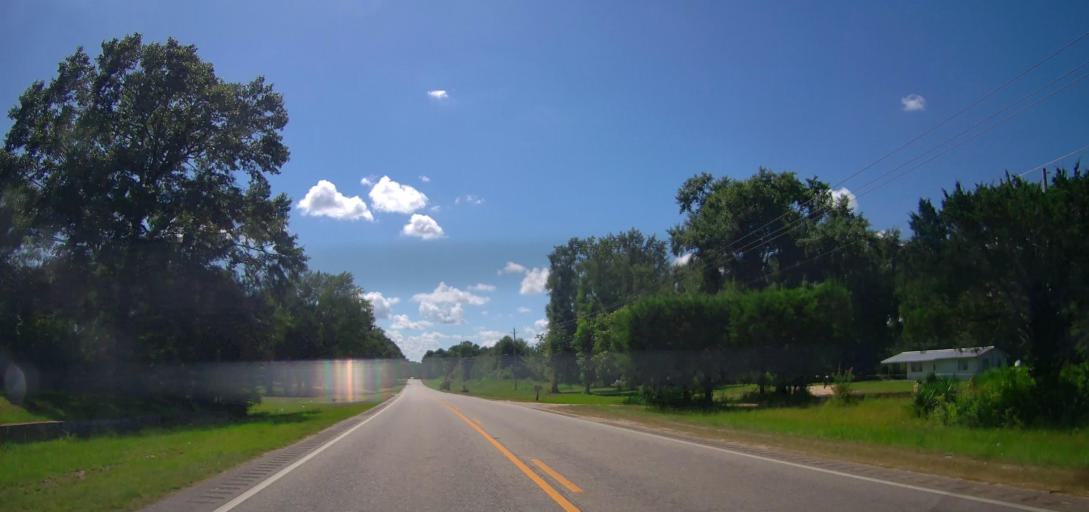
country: US
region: Alabama
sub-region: Elmore County
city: Tallassee
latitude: 32.3779
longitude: -85.8577
